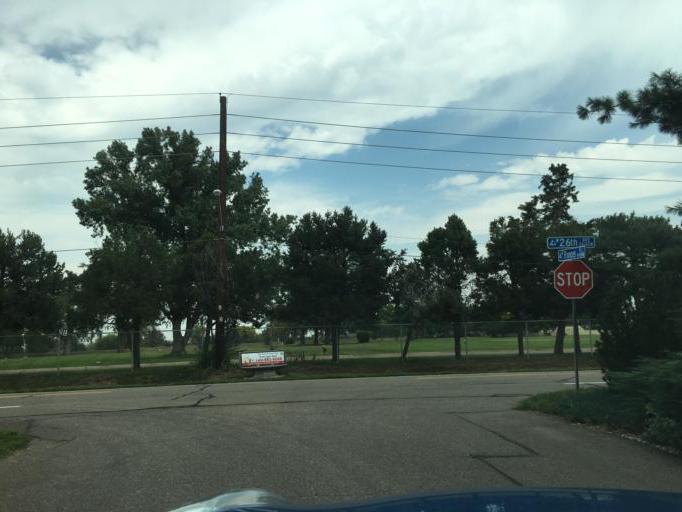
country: US
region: Colorado
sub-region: Jefferson County
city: Wheat Ridge
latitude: 39.7545
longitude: -105.0974
